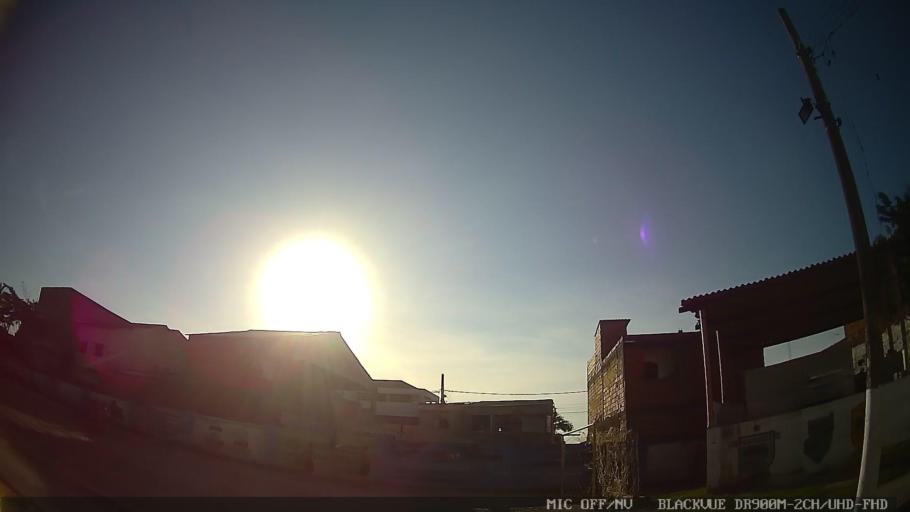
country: BR
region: Sao Paulo
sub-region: Guaruja
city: Guaruja
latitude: -23.9688
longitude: -46.2451
